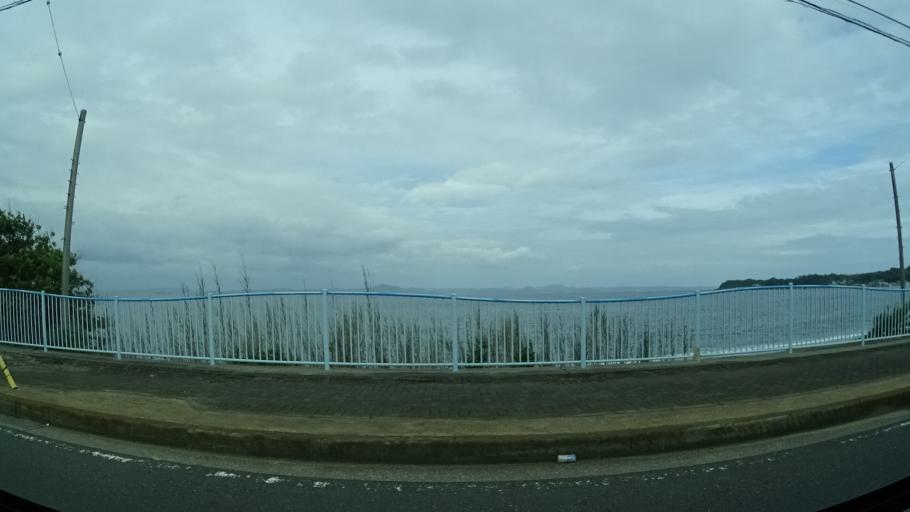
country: JP
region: Kanagawa
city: Miura
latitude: 35.1692
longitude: 139.6593
